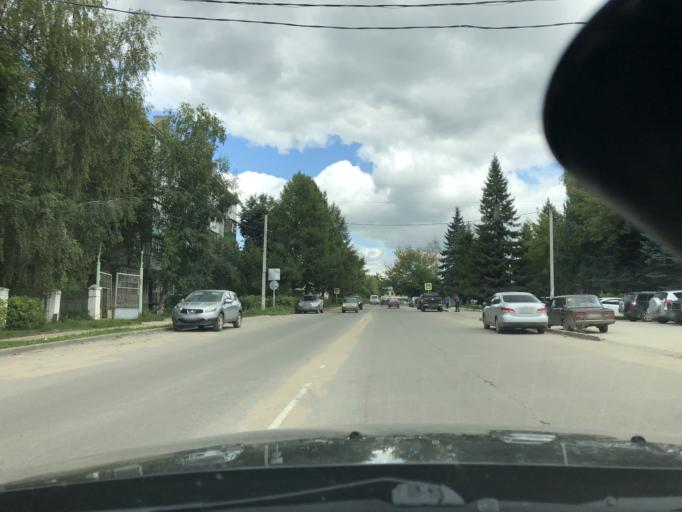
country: RU
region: Tula
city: Yasnogorsk
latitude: 54.4797
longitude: 37.6975
